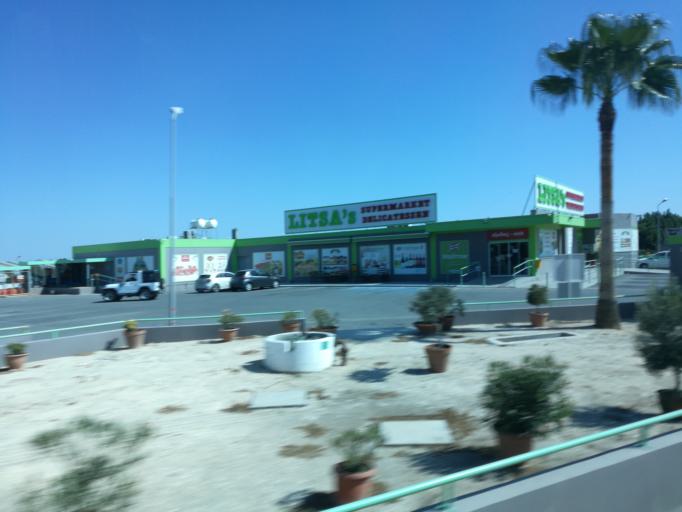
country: CY
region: Ammochostos
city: Acheritou
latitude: 35.0841
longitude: 33.8780
